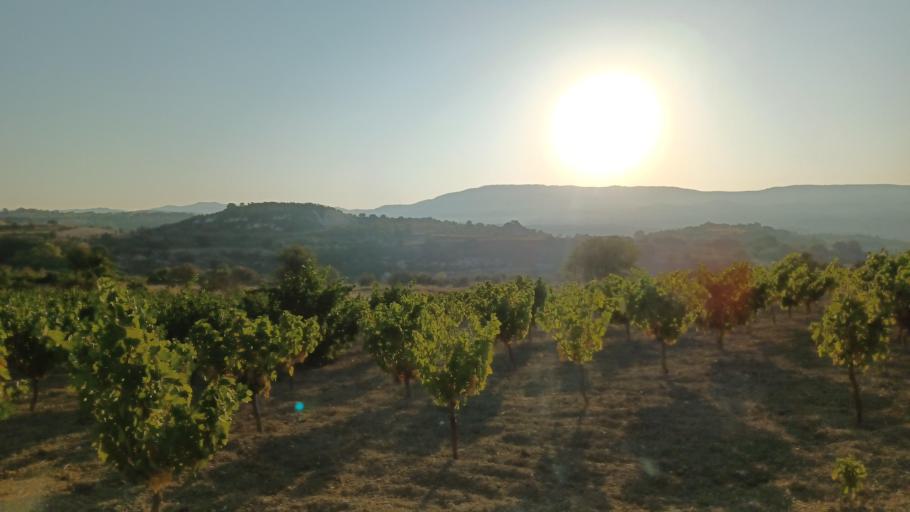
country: CY
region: Pafos
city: Mesogi
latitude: 34.8725
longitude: 32.5108
